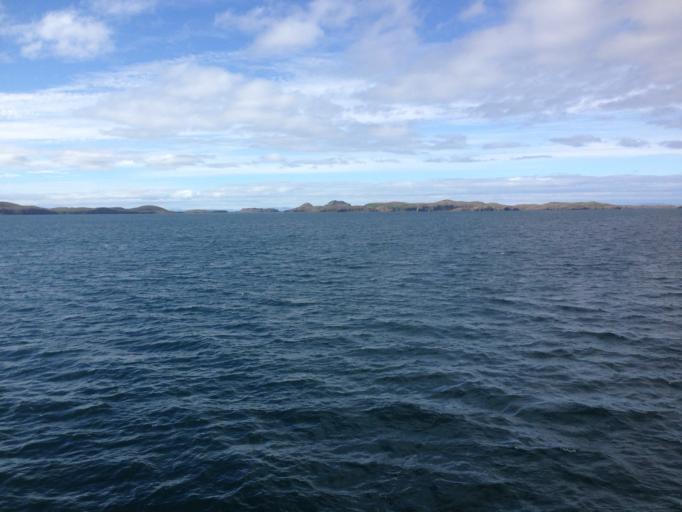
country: IS
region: West
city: Stykkisholmur
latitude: 65.1066
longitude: -22.5508
